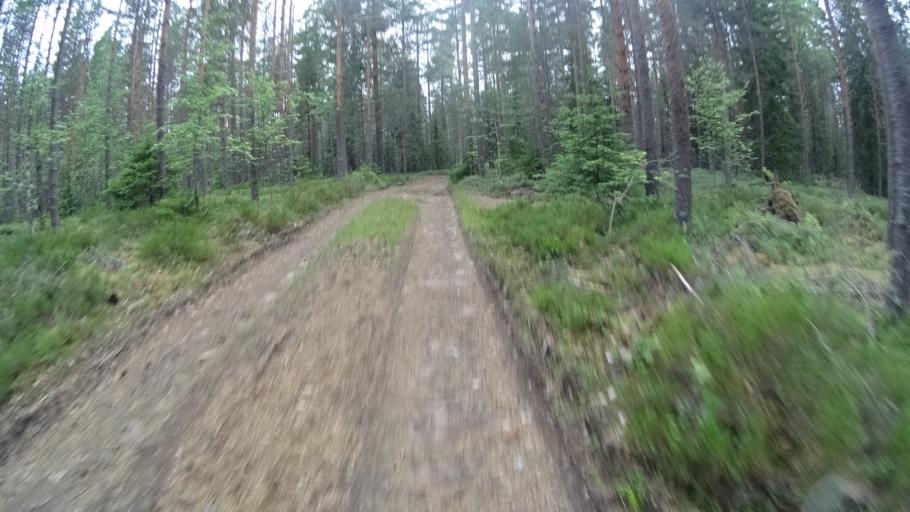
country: FI
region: Uusimaa
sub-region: Helsinki
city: Karkkila
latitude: 60.6023
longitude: 24.1586
